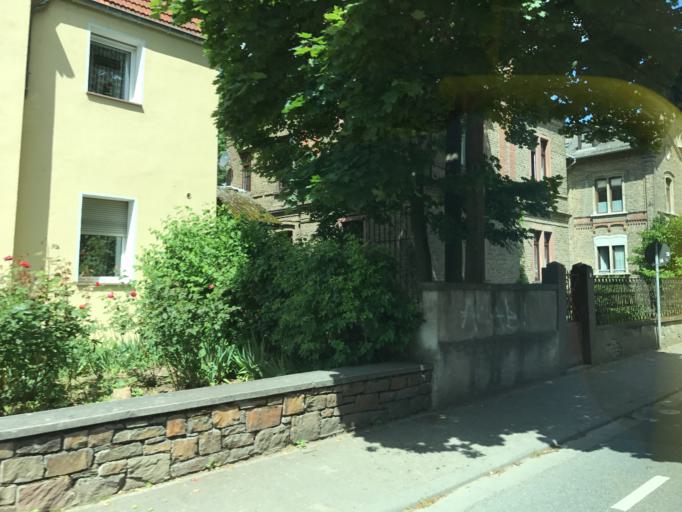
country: DE
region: Hesse
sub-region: Regierungsbezirk Darmstadt
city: Eltville
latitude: 50.0287
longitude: 8.1179
